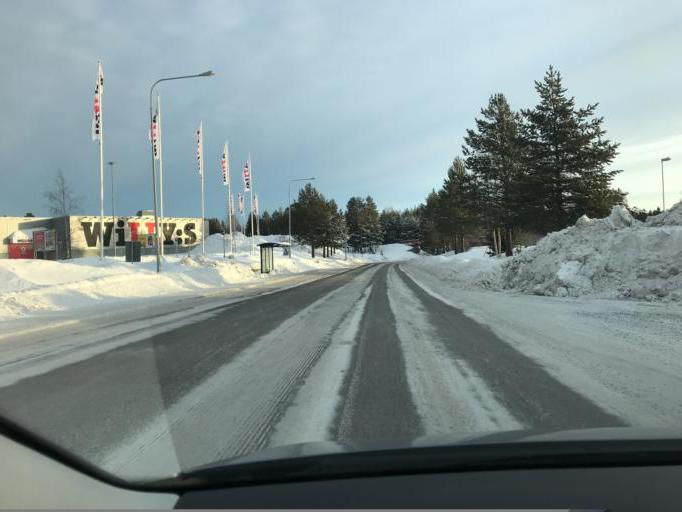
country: SE
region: Norrbotten
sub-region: Lulea Kommun
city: Gammelstad
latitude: 65.6194
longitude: 22.0528
